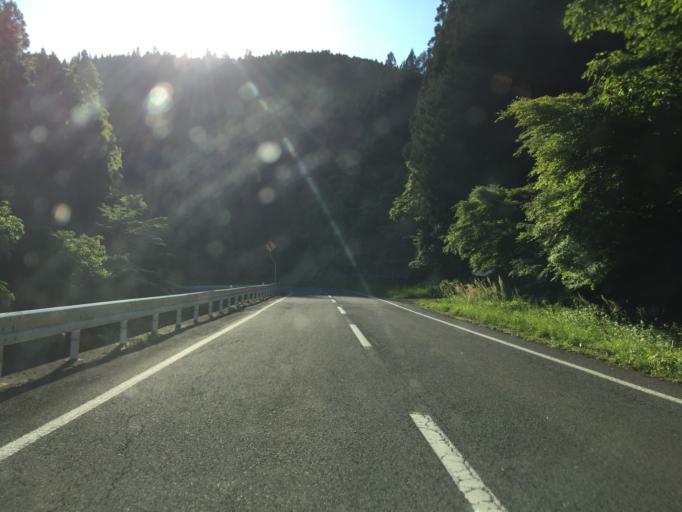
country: JP
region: Ibaraki
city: Daigo
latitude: 36.9279
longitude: 140.4821
